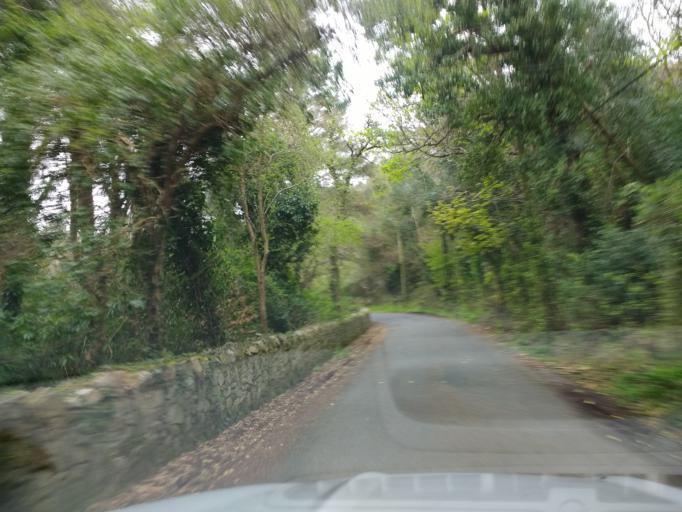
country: IE
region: Ulster
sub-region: County Donegal
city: Buncrana
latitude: 55.2201
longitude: -7.6118
